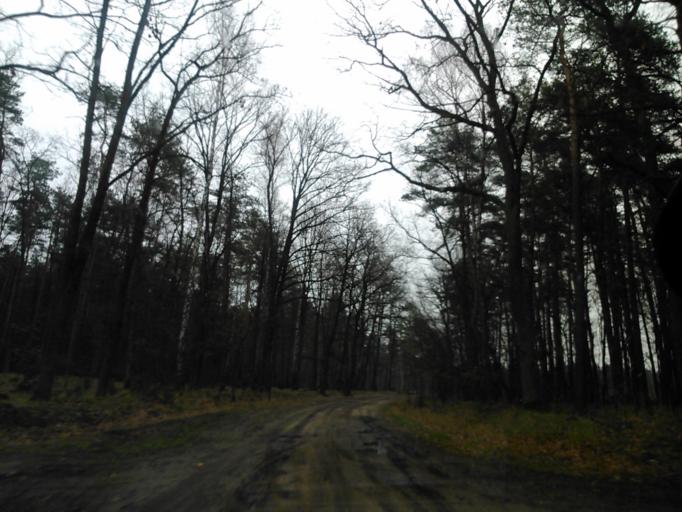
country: PL
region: Kujawsko-Pomorskie
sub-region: Powiat golubsko-dobrzynski
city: Radomin
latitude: 53.1341
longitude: 19.1429
